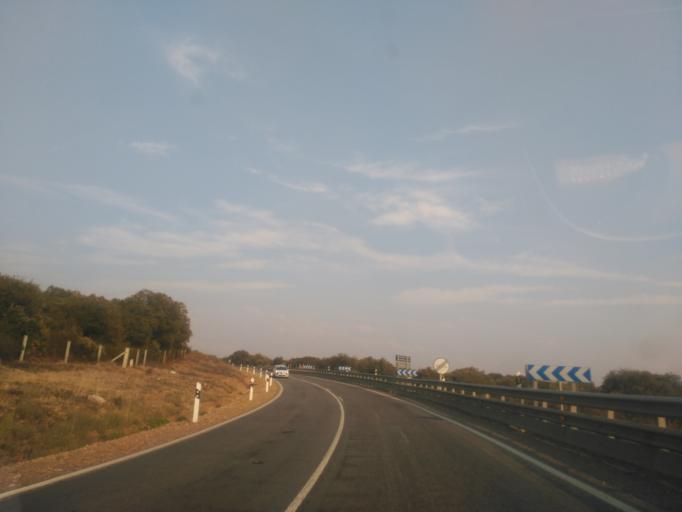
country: ES
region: Castille and Leon
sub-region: Provincia de Zamora
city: Perilla de Castro
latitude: 41.7492
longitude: -5.8540
